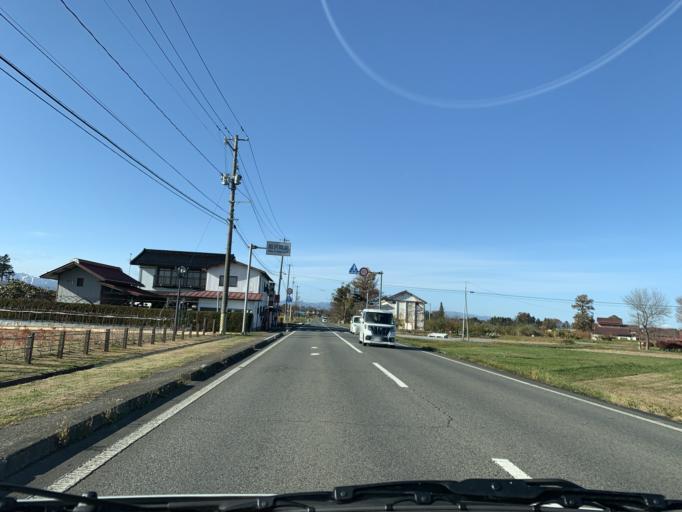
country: JP
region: Iwate
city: Mizusawa
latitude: 39.1782
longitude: 141.1354
